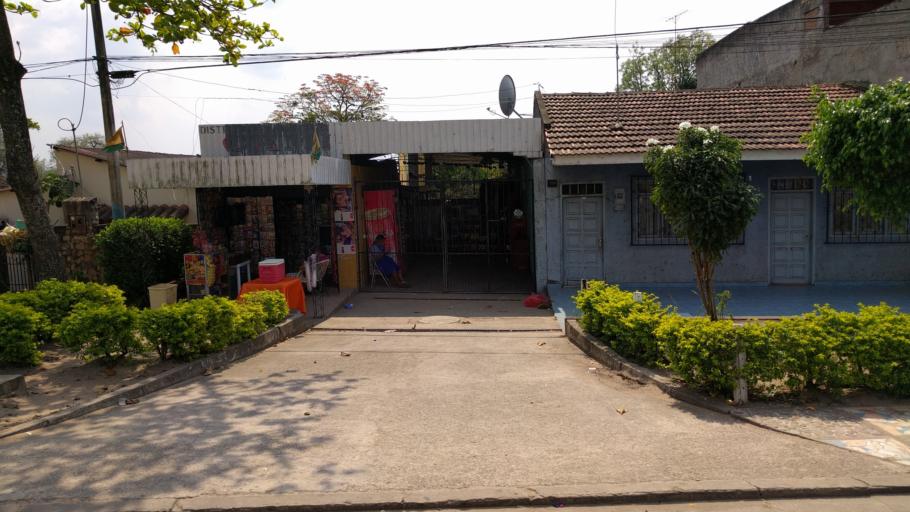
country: BO
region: Santa Cruz
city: Santa Rita
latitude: -17.8932
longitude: -63.3304
